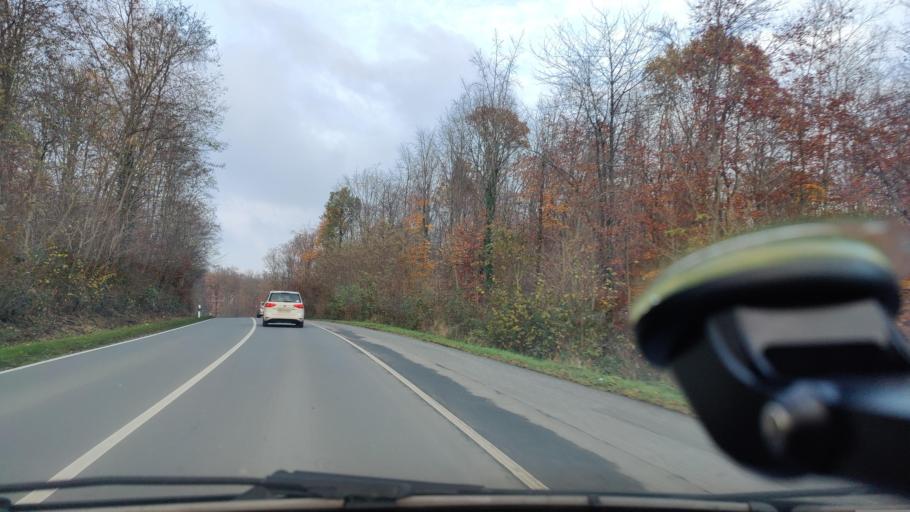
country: DE
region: North Rhine-Westphalia
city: Lunen
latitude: 51.6441
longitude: 7.5328
